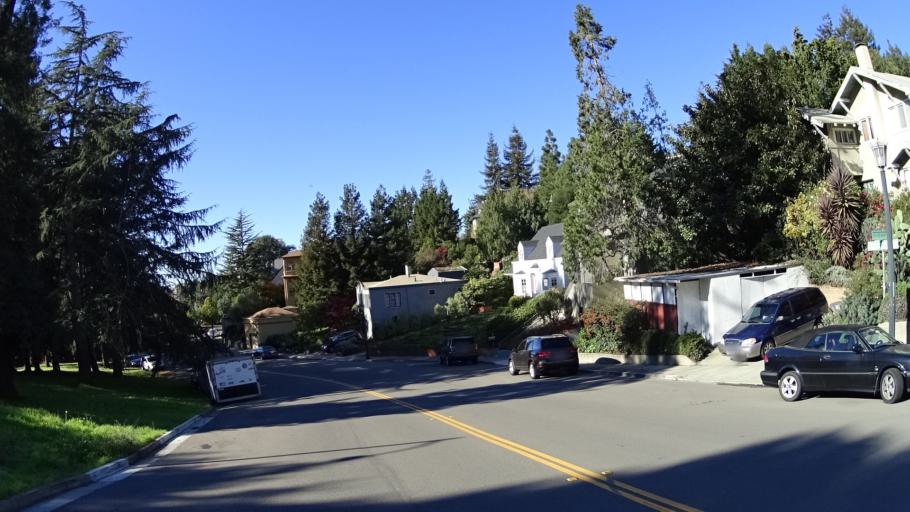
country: US
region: California
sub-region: Alameda County
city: Piedmont
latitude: 37.8429
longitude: -122.2319
